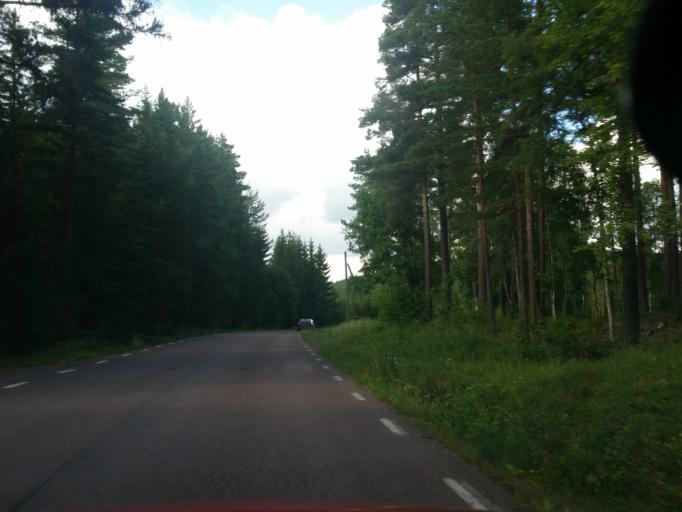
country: SE
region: Dalarna
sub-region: Gagnefs Kommun
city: Gagnef
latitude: 60.6762
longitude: 15.1716
